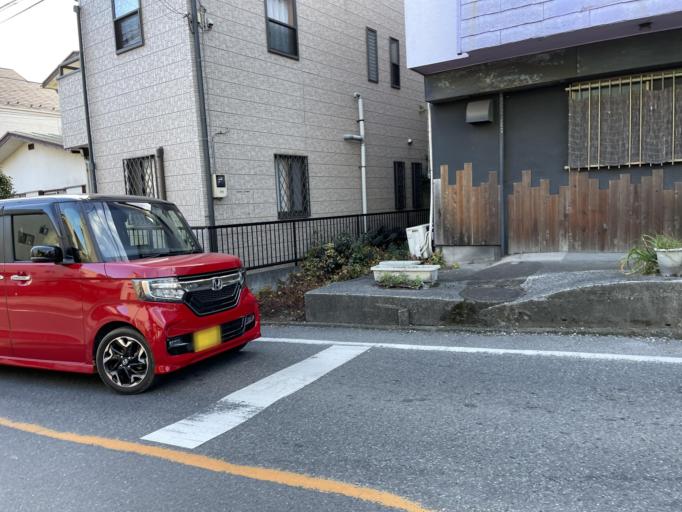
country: JP
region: Saitama
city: Wako
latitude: 35.7911
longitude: 139.6353
